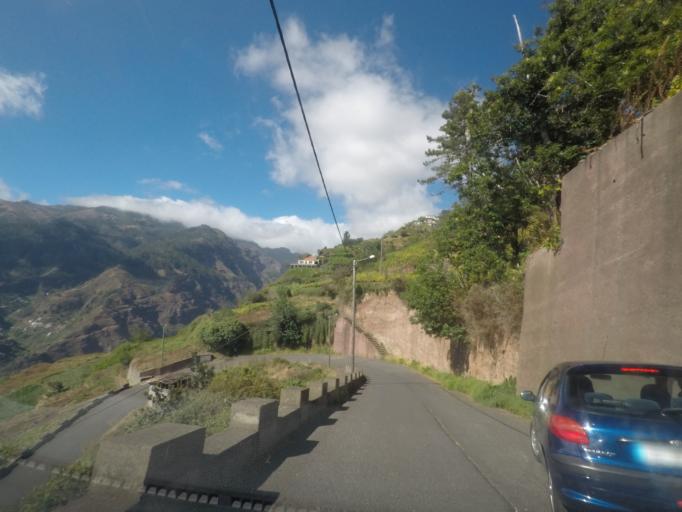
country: PT
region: Madeira
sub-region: Ribeira Brava
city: Campanario
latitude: 32.6926
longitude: -17.0368
